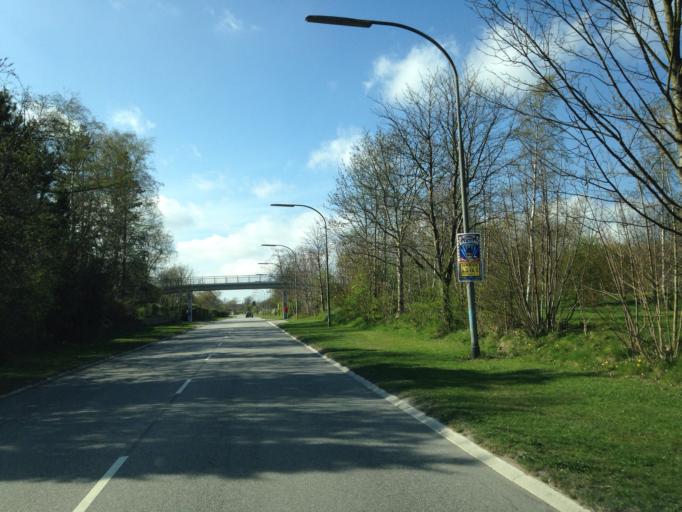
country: DK
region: Zealand
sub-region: Greve Kommune
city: Greve
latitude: 55.5829
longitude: 12.2824
